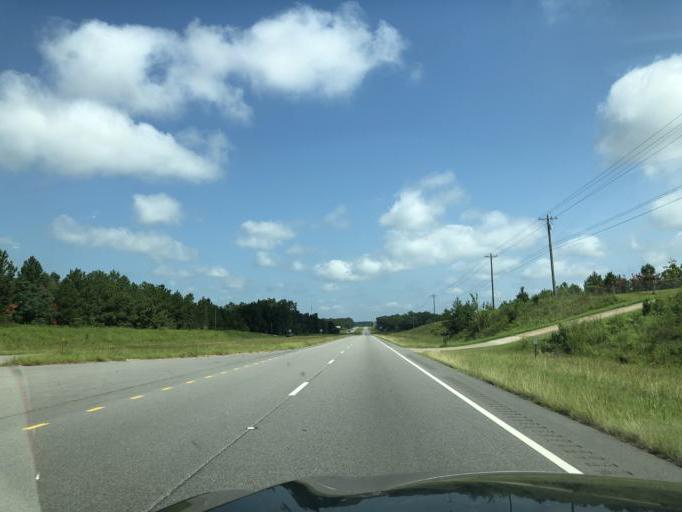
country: US
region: Alabama
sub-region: Houston County
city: Rehobeth
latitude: 31.0478
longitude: -85.4058
